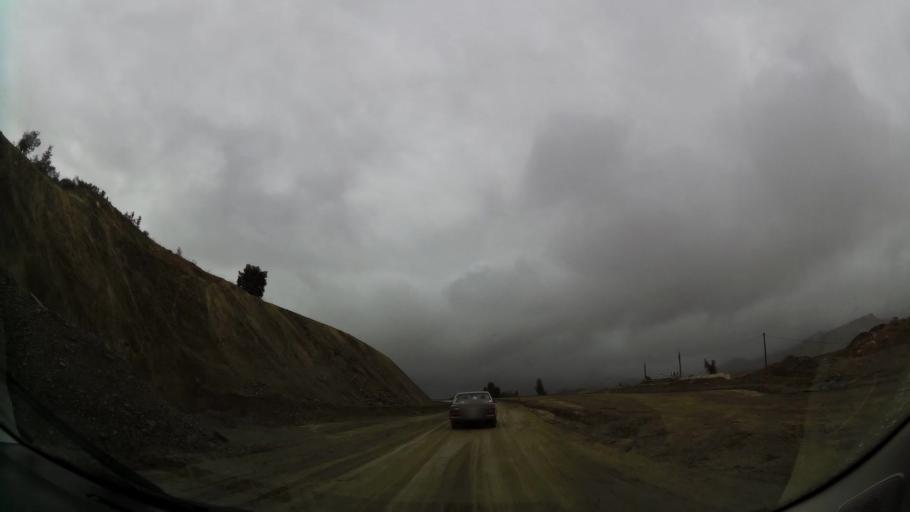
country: MA
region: Oriental
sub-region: Nador
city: Midar
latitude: 34.8969
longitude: -3.7738
